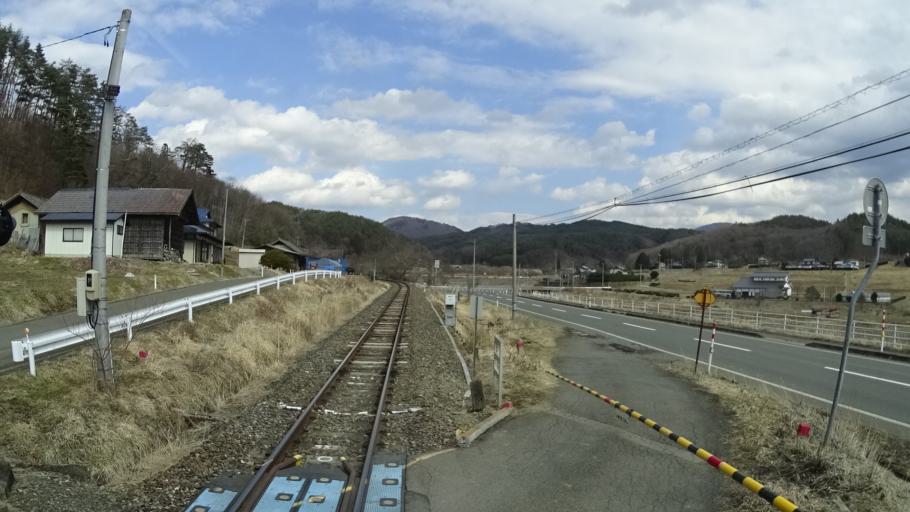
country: JP
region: Iwate
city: Tono
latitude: 39.3532
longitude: 141.3384
